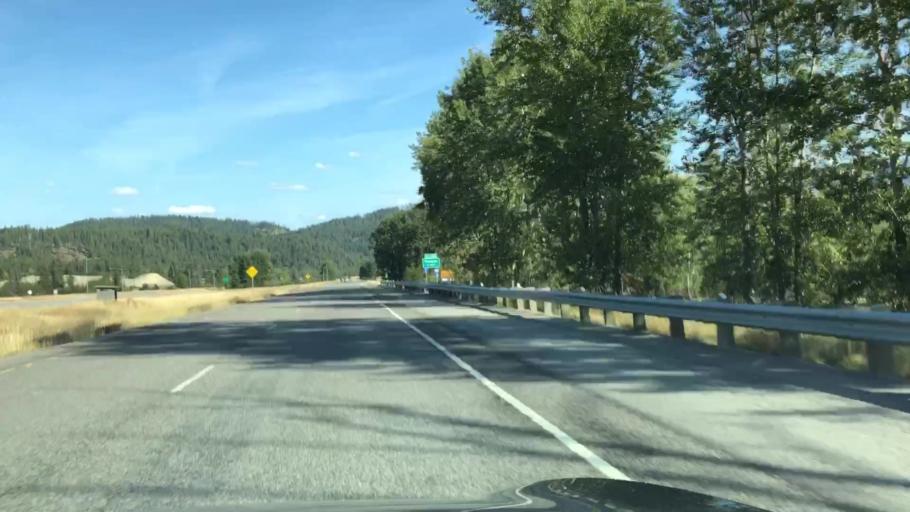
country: US
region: Montana
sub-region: Sanders County
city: Thompson Falls
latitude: 47.3931
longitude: -115.4241
